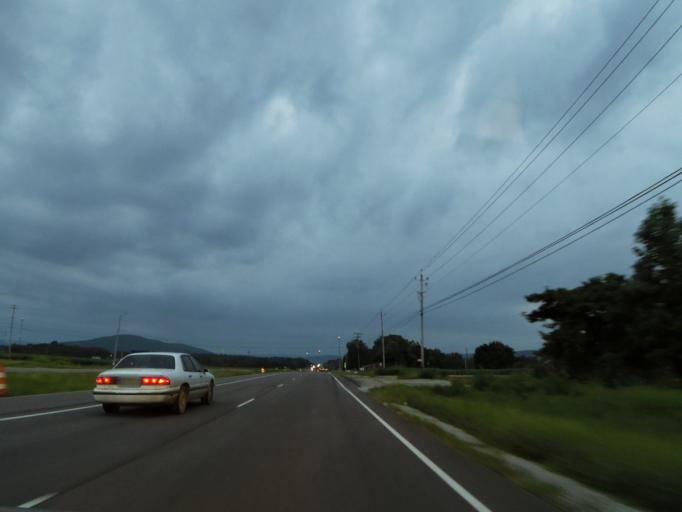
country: US
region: Alabama
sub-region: Madison County
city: Moores Mill
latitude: 34.7593
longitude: -86.4759
